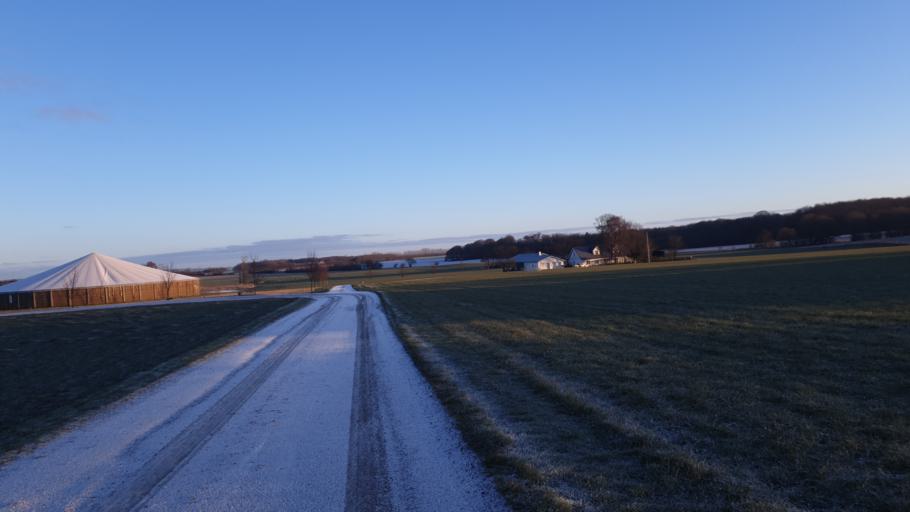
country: DK
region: Central Jutland
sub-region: Hedensted Kommune
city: Hedensted
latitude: 55.8182
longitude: 9.7007
